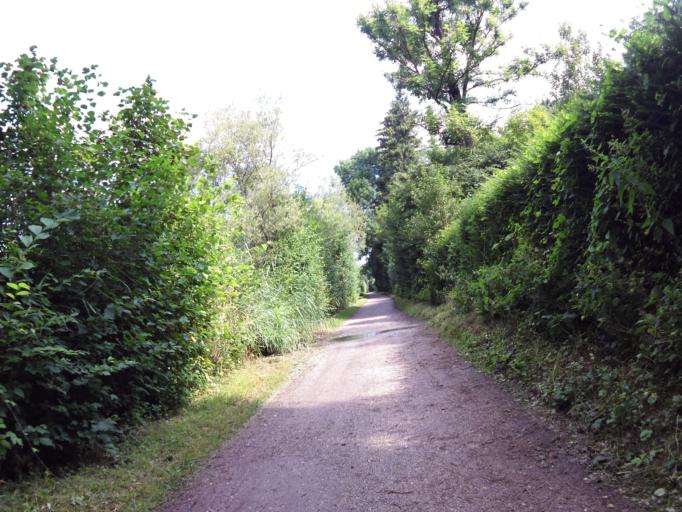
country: DE
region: Bavaria
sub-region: Upper Bavaria
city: Andechs
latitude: 47.9762
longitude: 11.1526
